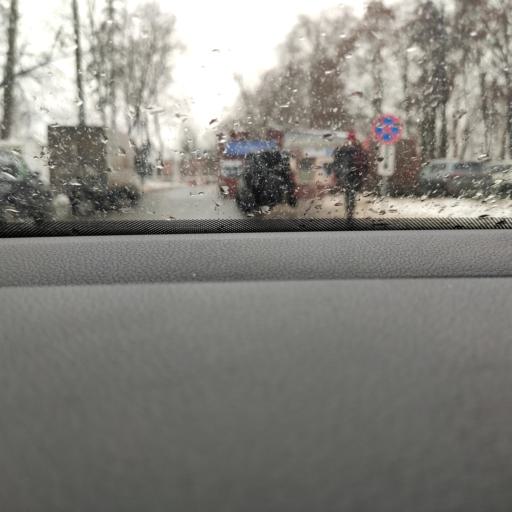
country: RU
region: Moscow
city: Novyye Cheremushki
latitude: 55.6981
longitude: 37.6087
